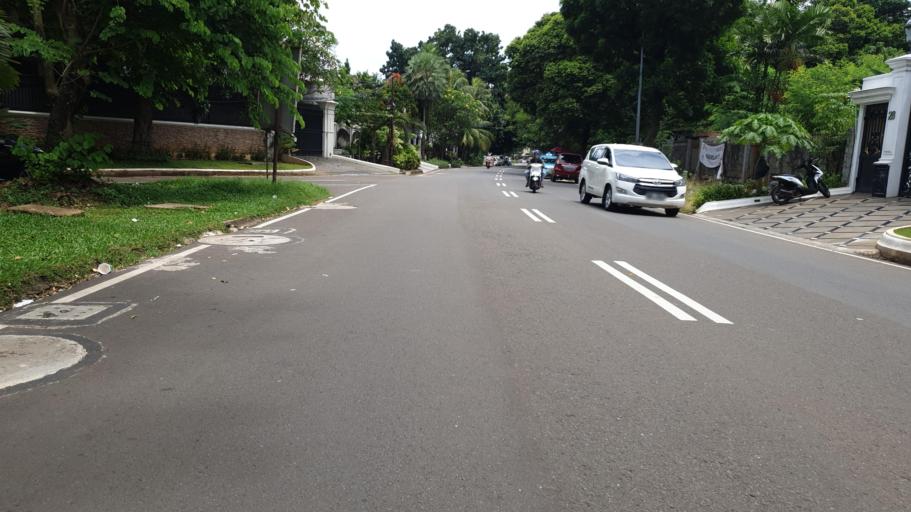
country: ID
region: Banten
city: South Tangerang
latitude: -6.2787
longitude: 106.7850
